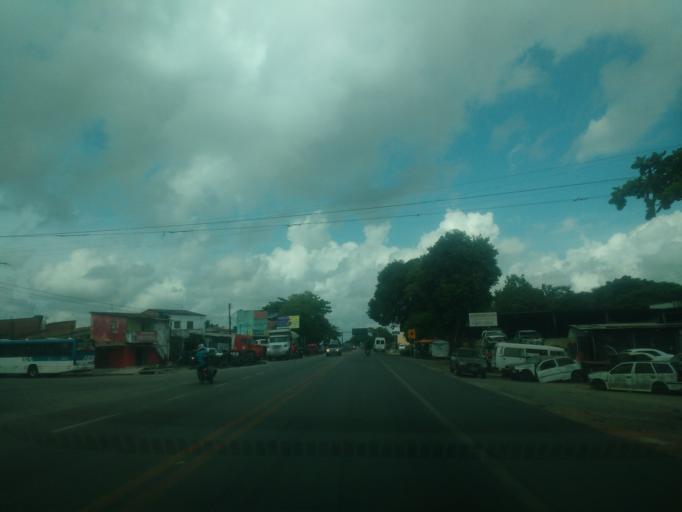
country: BR
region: Alagoas
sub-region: Satuba
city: Satuba
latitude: -9.5654
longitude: -35.7903
